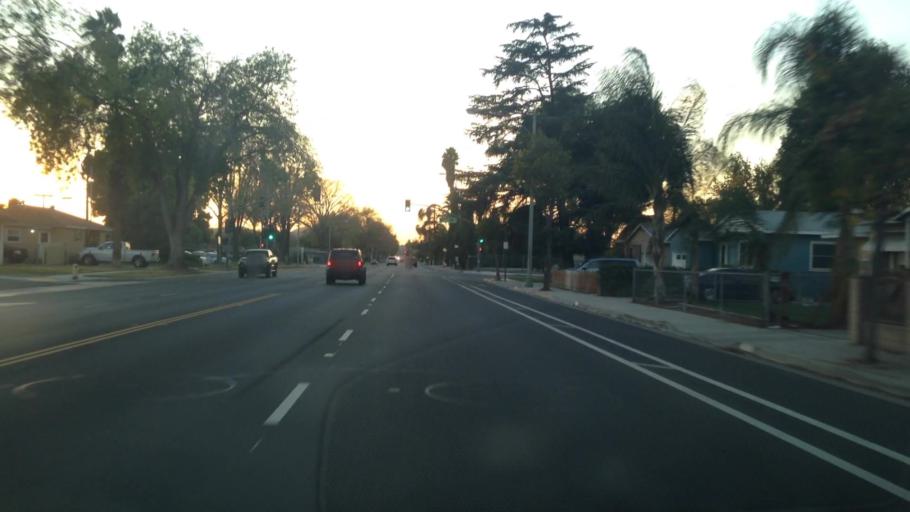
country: US
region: California
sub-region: Riverside County
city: Riverside
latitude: 33.9535
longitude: -117.4089
